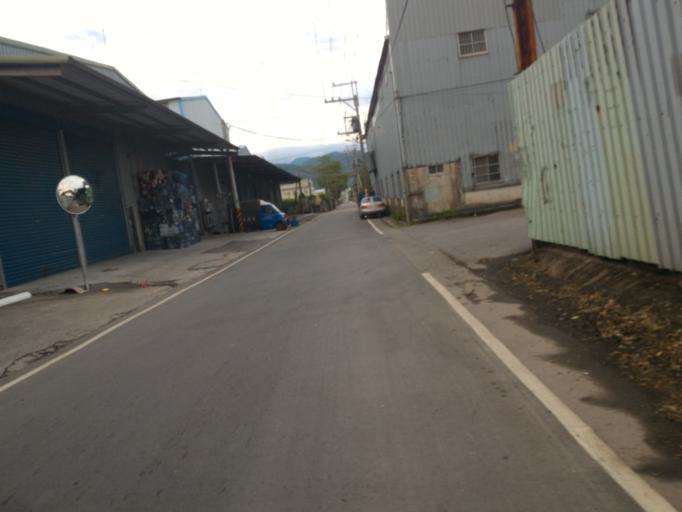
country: TW
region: Taiwan
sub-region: Taoyuan
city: Taoyuan
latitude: 24.9568
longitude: 121.4002
